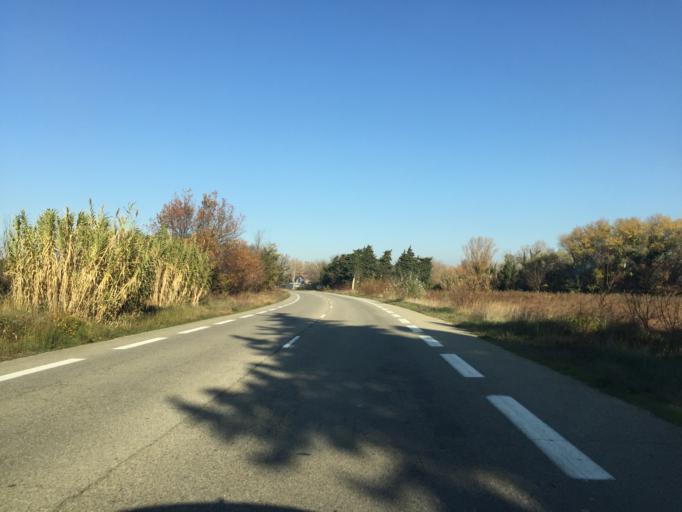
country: FR
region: Provence-Alpes-Cote d'Azur
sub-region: Departement du Vaucluse
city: Jonquieres
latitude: 44.1142
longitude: 4.9241
